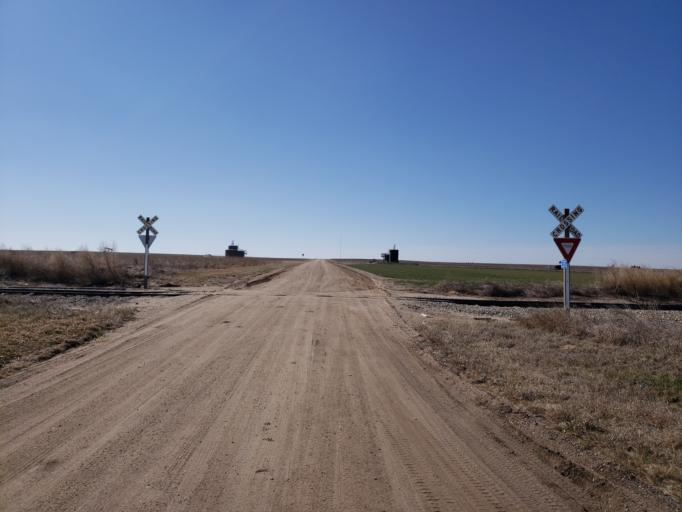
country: US
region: Kansas
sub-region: Ness County
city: Ness City
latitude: 38.4517
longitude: -99.9538
